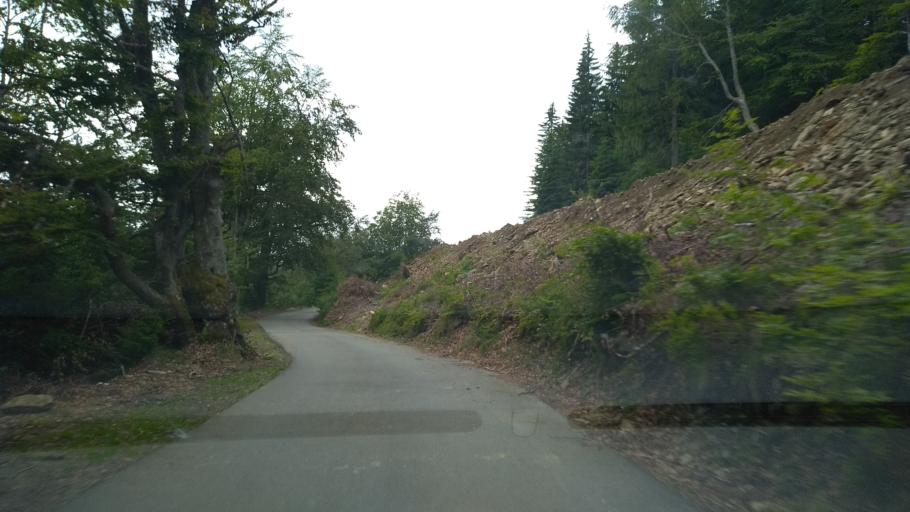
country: RO
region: Hunedoara
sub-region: Municipiul  Vulcan
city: Jiu-Paroseni
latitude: 45.3232
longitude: 23.2928
